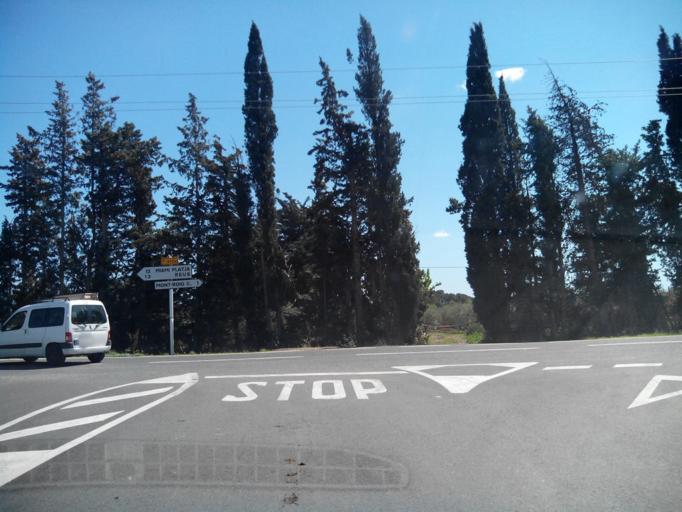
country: ES
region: Catalonia
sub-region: Provincia de Tarragona
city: Riudecanyes
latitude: 41.0963
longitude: 0.9711
